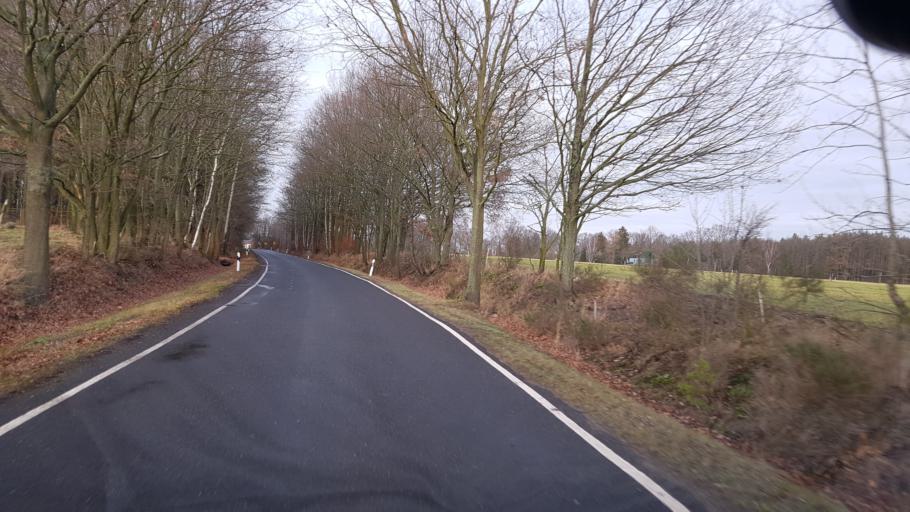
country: DE
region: Brandenburg
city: Altdobern
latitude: 51.6600
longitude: 13.9968
